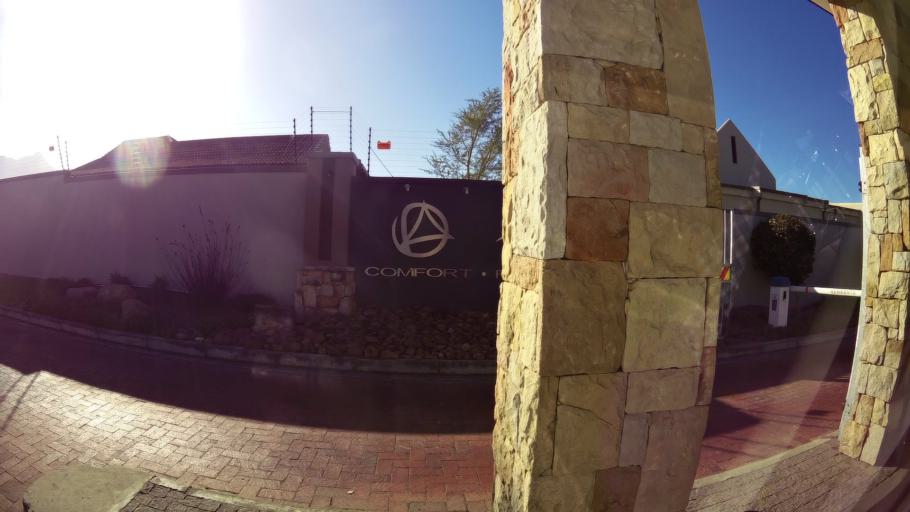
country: ZA
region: Western Cape
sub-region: Eden District Municipality
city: George
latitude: -33.9616
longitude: 22.4248
